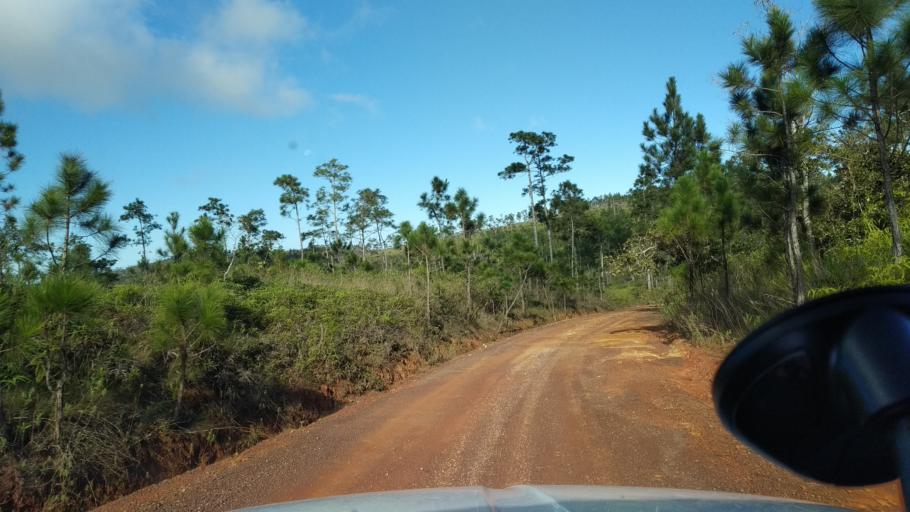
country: BZ
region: Cayo
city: Belmopan
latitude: 16.9951
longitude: -88.8283
